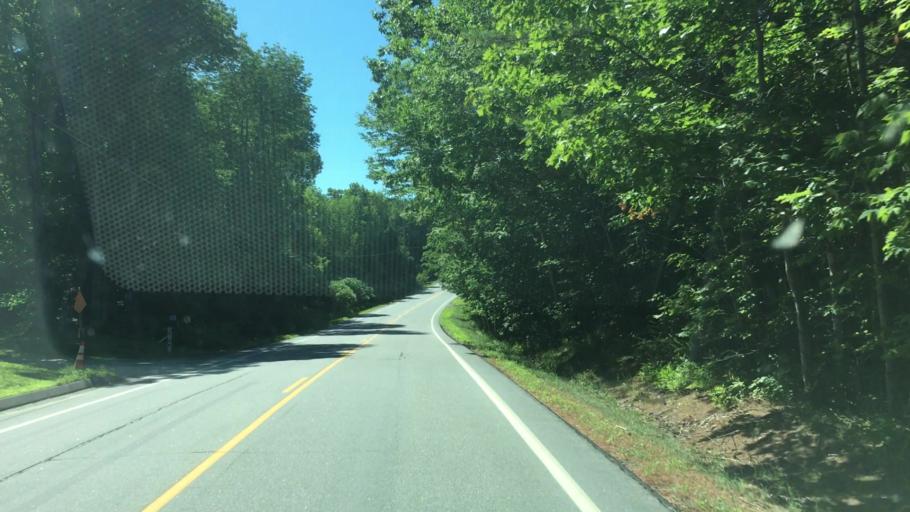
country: US
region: Maine
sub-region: Hancock County
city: Orland
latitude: 44.5391
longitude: -68.6816
